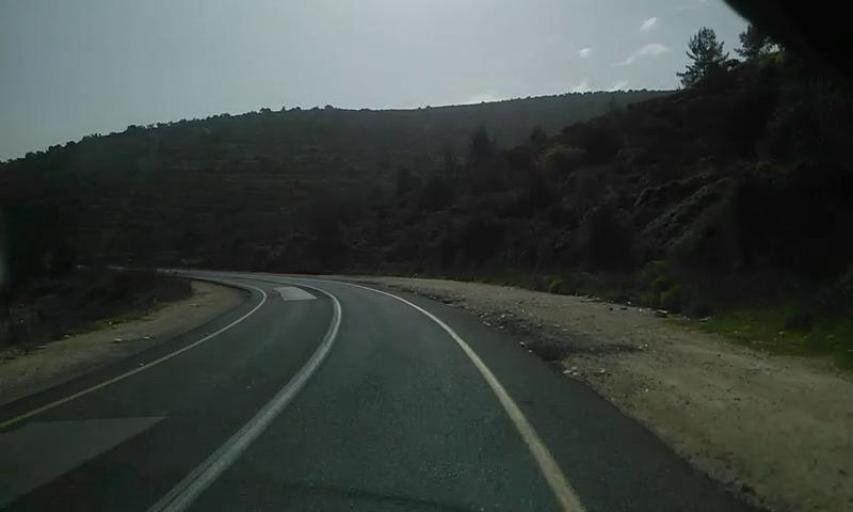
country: PS
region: West Bank
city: `Atarah
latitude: 31.9994
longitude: 35.2340
